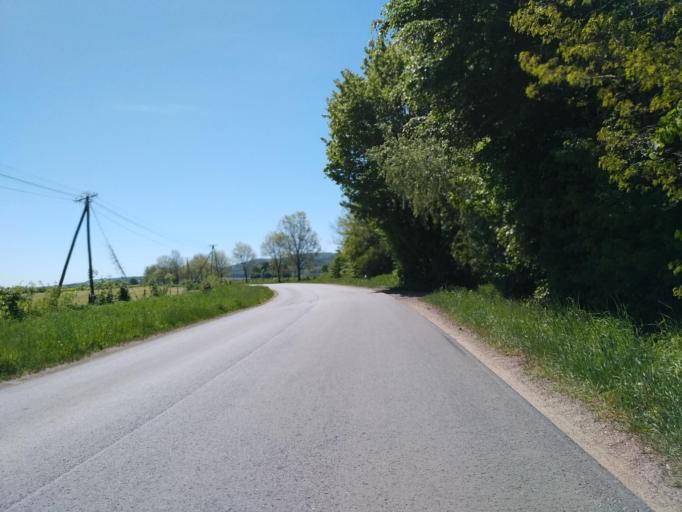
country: PL
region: Subcarpathian Voivodeship
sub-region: Powiat krosnienski
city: Sieniawa
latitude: 49.5550
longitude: 21.9367
